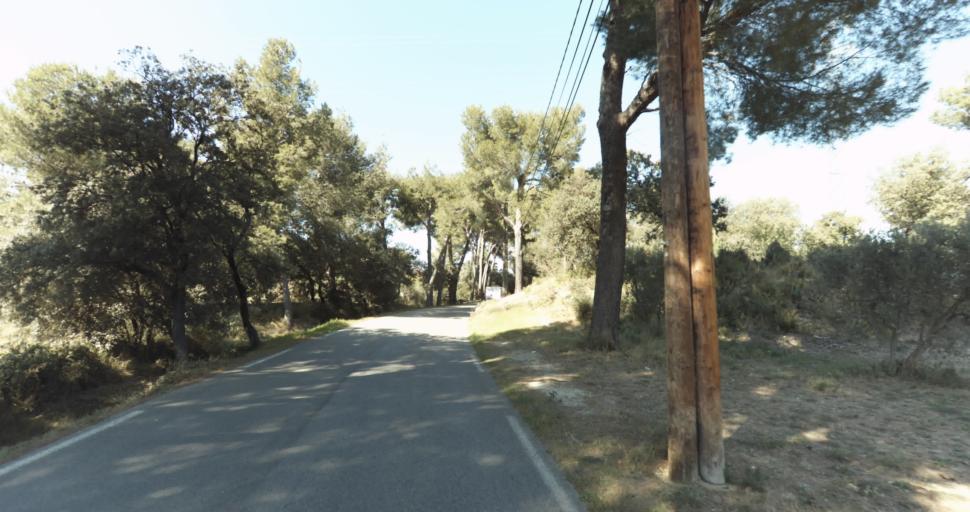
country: FR
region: Provence-Alpes-Cote d'Azur
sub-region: Departement des Bouches-du-Rhone
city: Pelissanne
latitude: 43.6436
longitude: 5.1810
